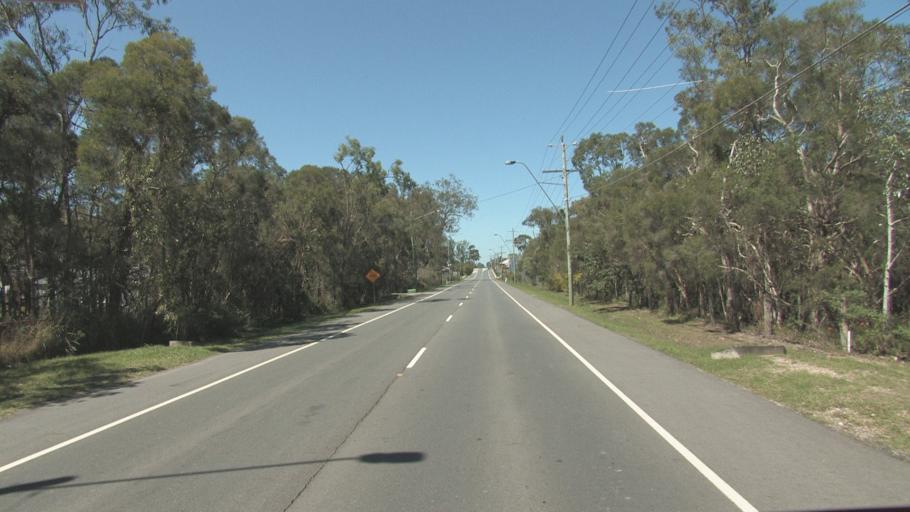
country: AU
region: Queensland
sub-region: Logan
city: Logan City
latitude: -27.6660
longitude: 153.0914
